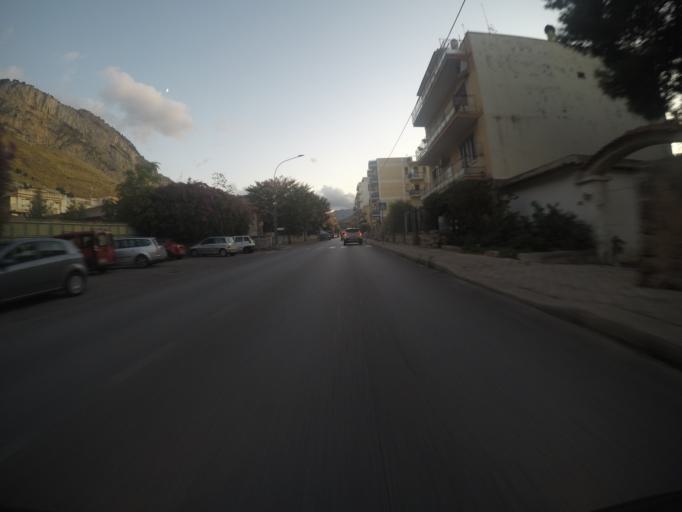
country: IT
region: Sicily
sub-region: Palermo
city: Capaci
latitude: 38.1774
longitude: 13.2433
